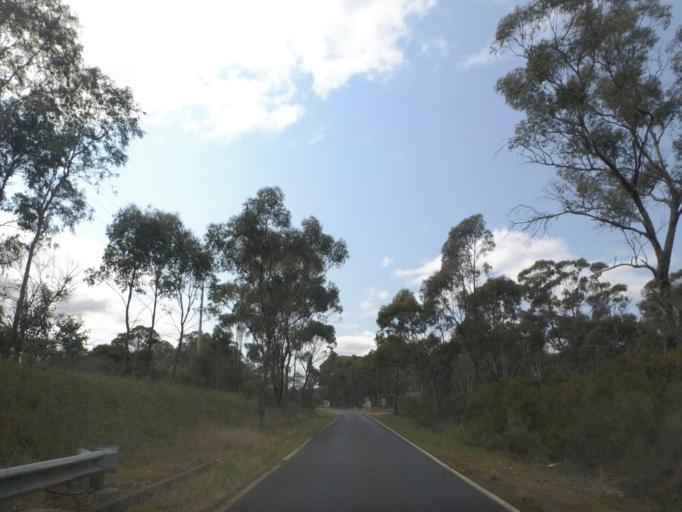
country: AU
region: Victoria
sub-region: Murrindindi
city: Kinglake West
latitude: -37.1076
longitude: 145.0923
